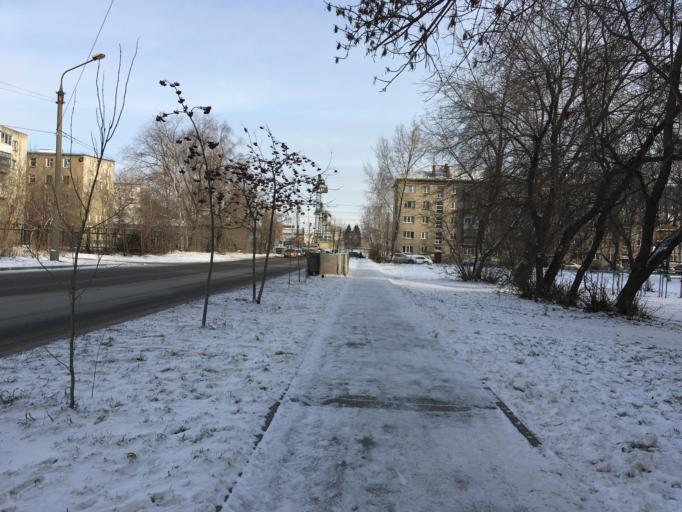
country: RU
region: Novosibirsk
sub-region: Novosibirskiy Rayon
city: Novosibirsk
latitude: 55.0585
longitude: 82.9741
